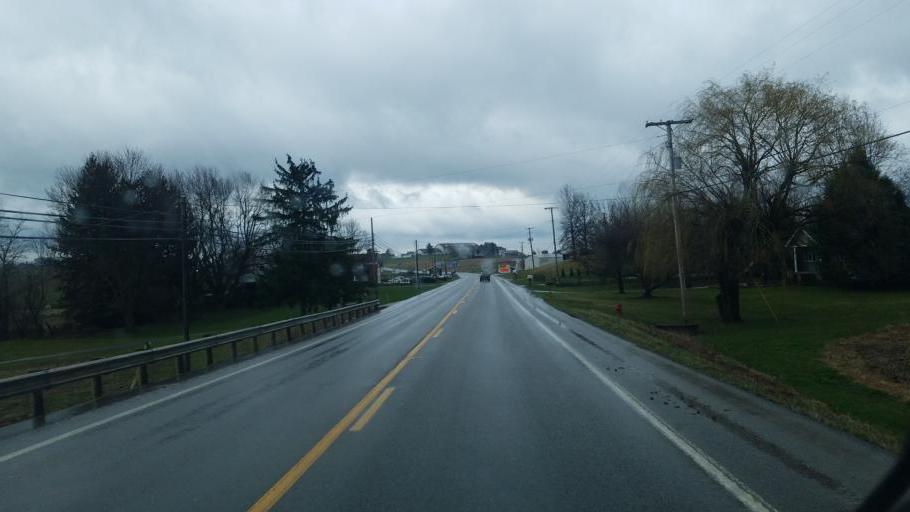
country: US
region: Ohio
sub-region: Holmes County
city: Millersburg
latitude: 40.5574
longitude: -81.7890
